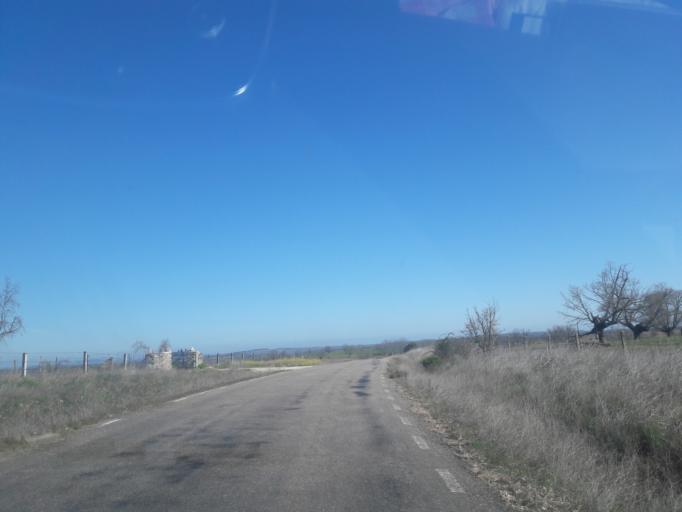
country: ES
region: Castille and Leon
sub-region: Provincia de Salamanca
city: Valsalabroso
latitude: 41.1340
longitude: -6.4827
